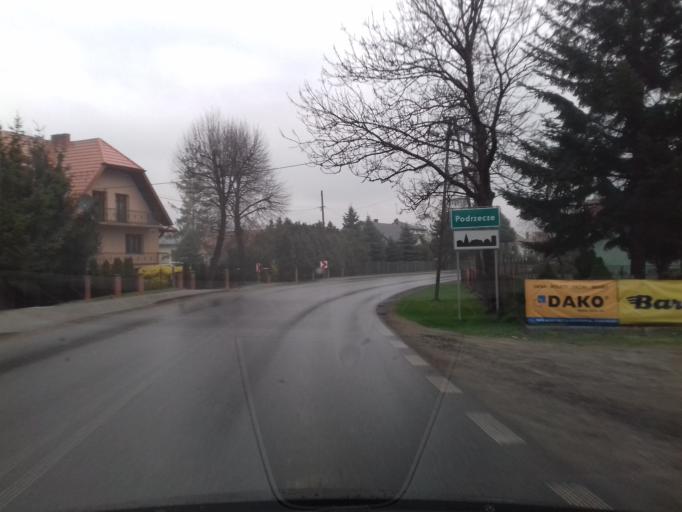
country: PL
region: Lesser Poland Voivodeship
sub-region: Powiat nowosadecki
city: Stary Sacz
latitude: 49.5982
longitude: 20.6366
